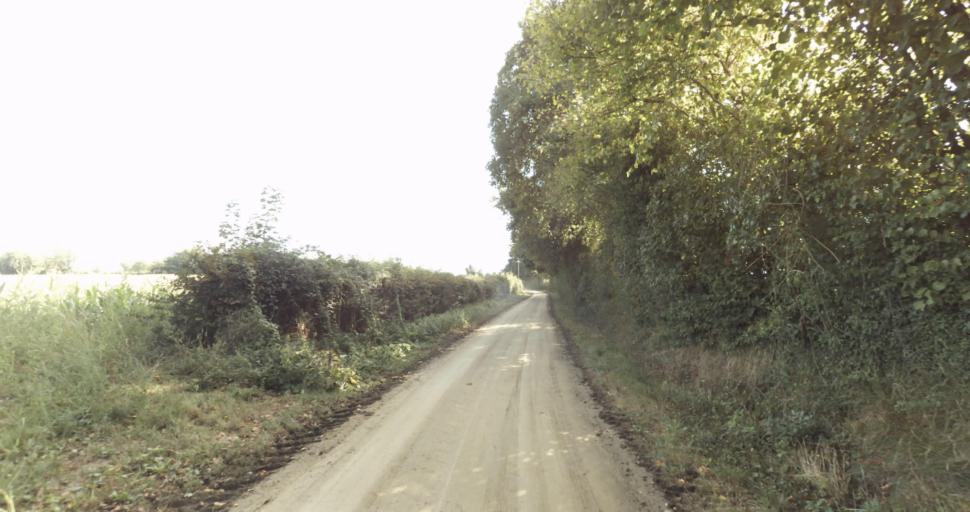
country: FR
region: Lower Normandy
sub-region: Departement de l'Orne
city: Vimoutiers
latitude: 48.9310
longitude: 0.1352
